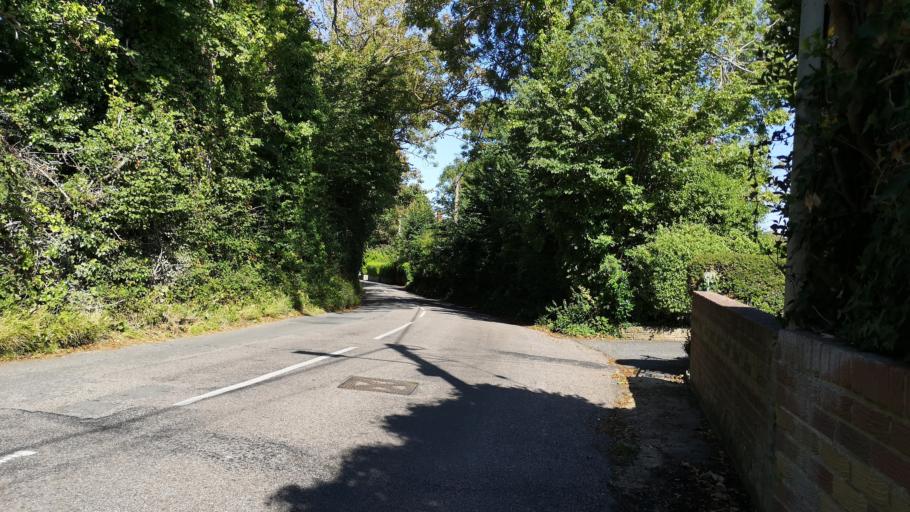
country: GB
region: England
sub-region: Isle of Wight
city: Totland
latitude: 50.6738
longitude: -1.5307
